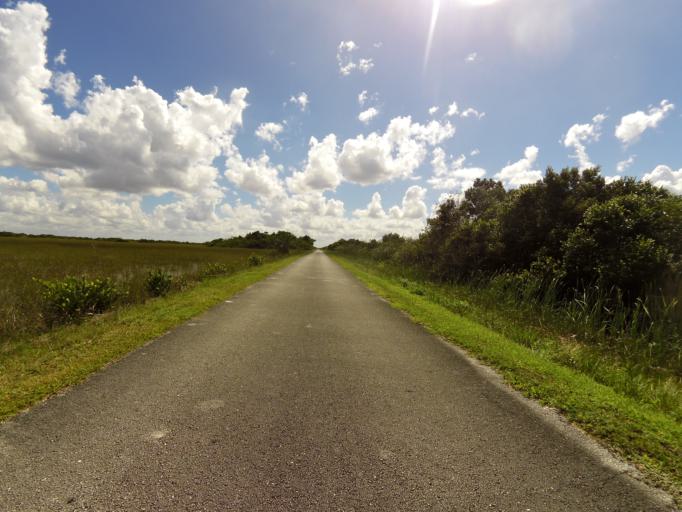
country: US
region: Florida
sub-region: Miami-Dade County
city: The Hammocks
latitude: 25.7109
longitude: -80.7668
